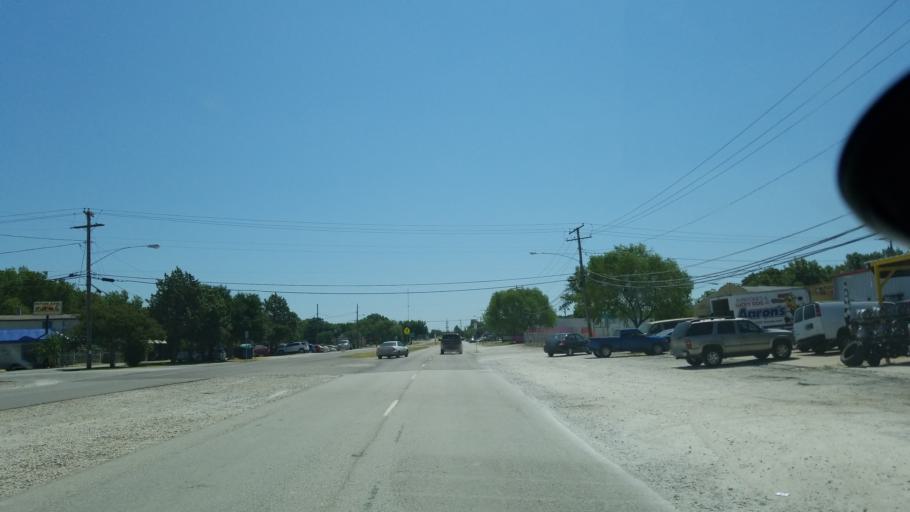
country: US
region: Texas
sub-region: Dallas County
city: Cockrell Hill
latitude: 32.7465
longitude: -96.9133
